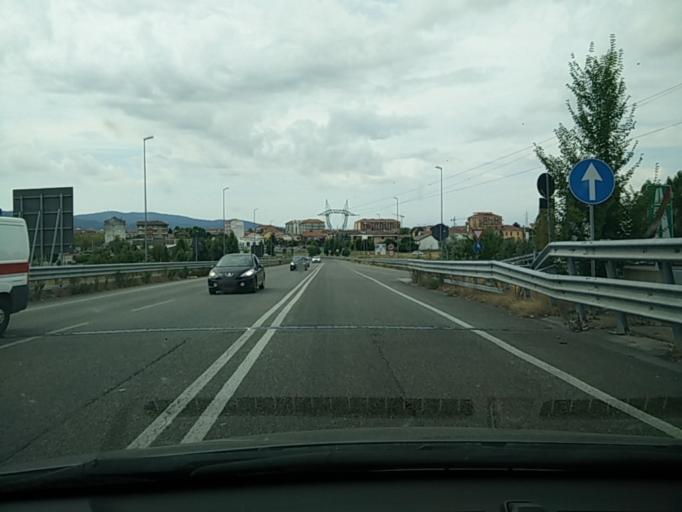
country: IT
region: Piedmont
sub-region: Provincia di Torino
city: Settimo Torinese
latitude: 45.1449
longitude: 7.7580
